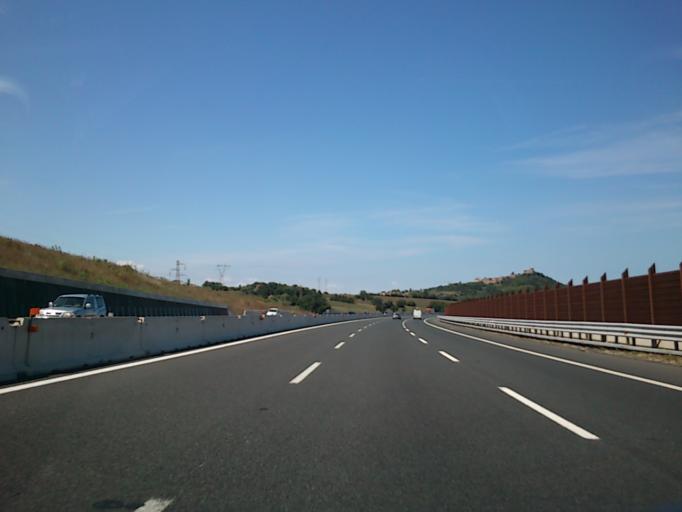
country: IT
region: The Marches
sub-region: Provincia di Pesaro e Urbino
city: Gradara
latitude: 43.9281
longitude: 12.7962
